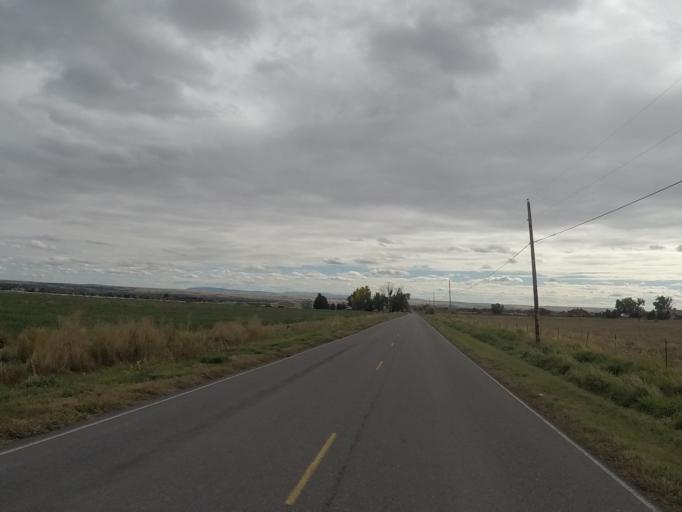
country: US
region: Montana
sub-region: Yellowstone County
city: Laurel
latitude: 45.7741
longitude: -108.6592
